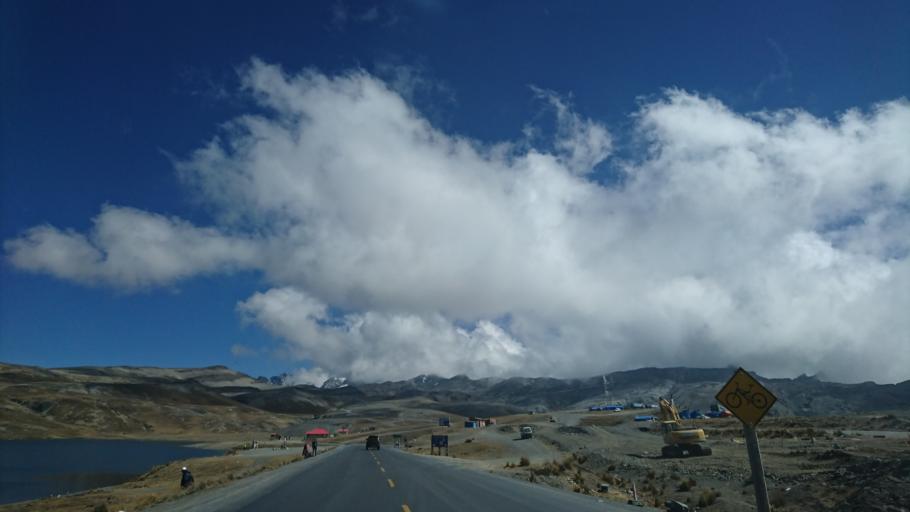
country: BO
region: La Paz
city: La Paz
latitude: -16.3394
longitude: -68.0389
